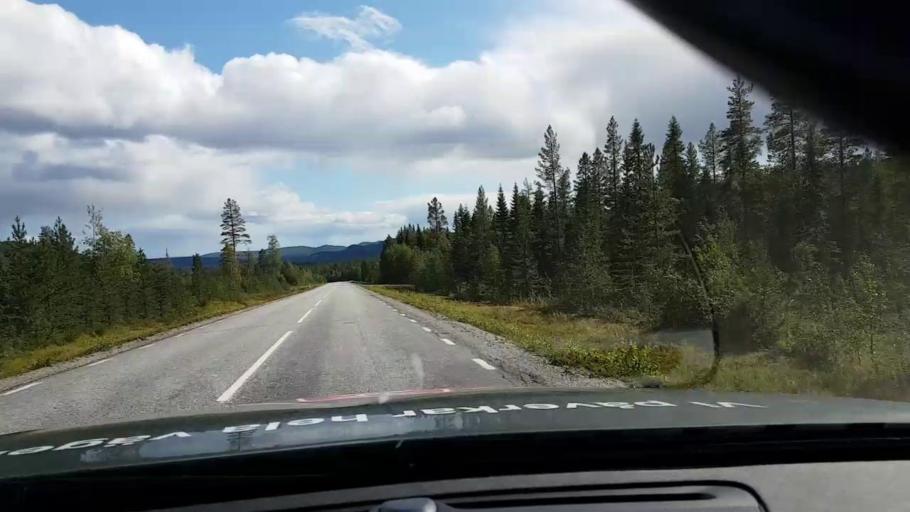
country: SE
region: Vaesterbotten
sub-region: Asele Kommun
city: Asele
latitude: 63.7682
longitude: 17.6831
